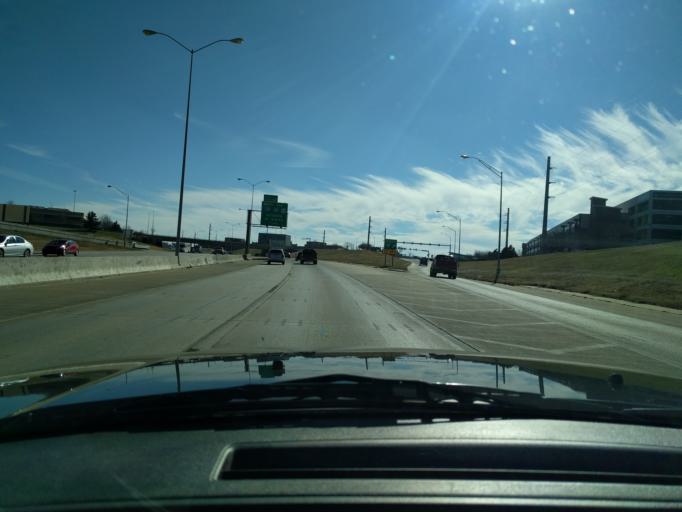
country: US
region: Oklahoma
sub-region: Oklahoma County
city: Oklahoma City
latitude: 35.4766
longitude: -97.5094
